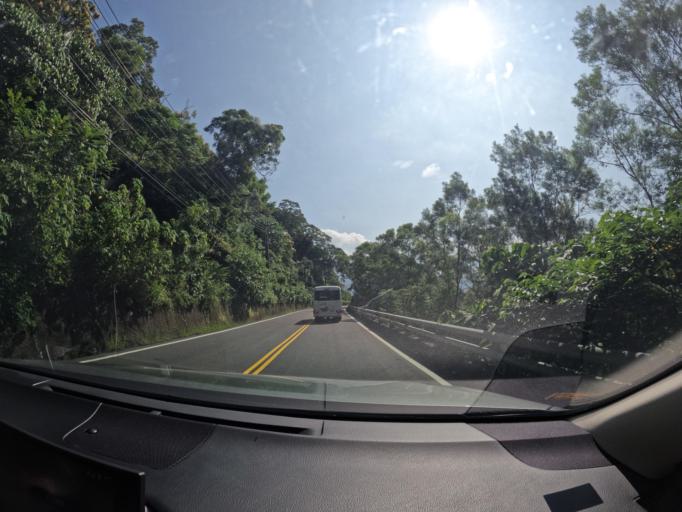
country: TW
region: Taiwan
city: Yujing
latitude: 23.0699
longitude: 120.6361
